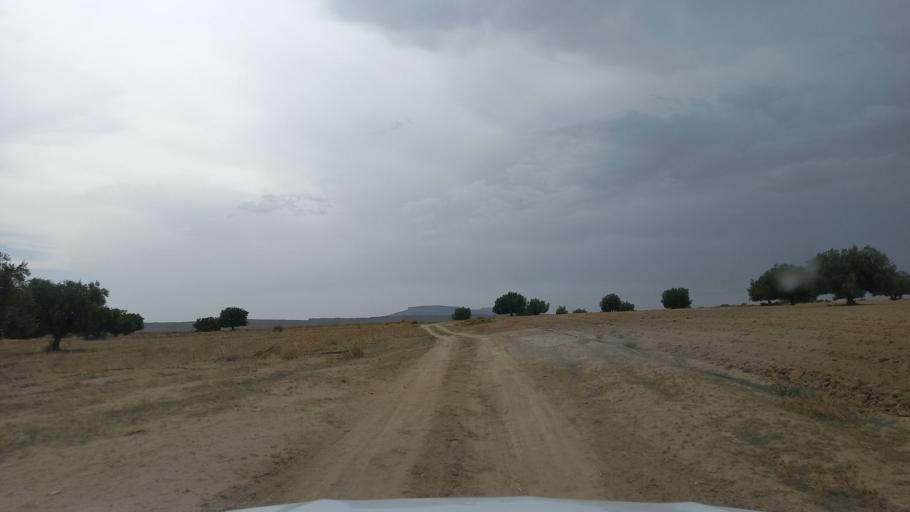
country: TN
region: Al Qasrayn
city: Kasserine
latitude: 35.2349
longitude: 9.0145
